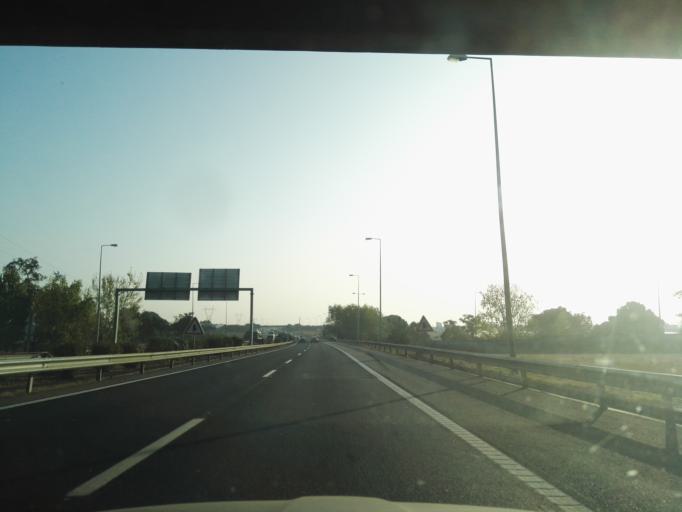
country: PT
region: Setubal
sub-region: Montijo
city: Montijo
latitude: 38.6790
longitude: -8.9450
